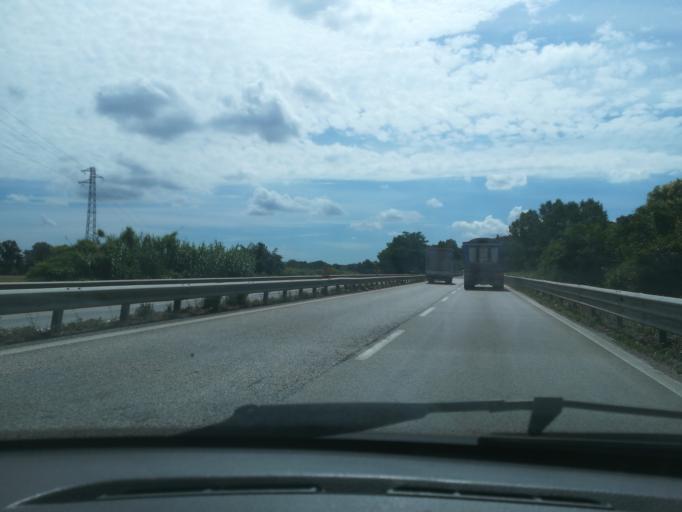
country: IT
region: The Marches
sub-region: Provincia di Macerata
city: Corridonia
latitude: 43.2663
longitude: 13.5260
